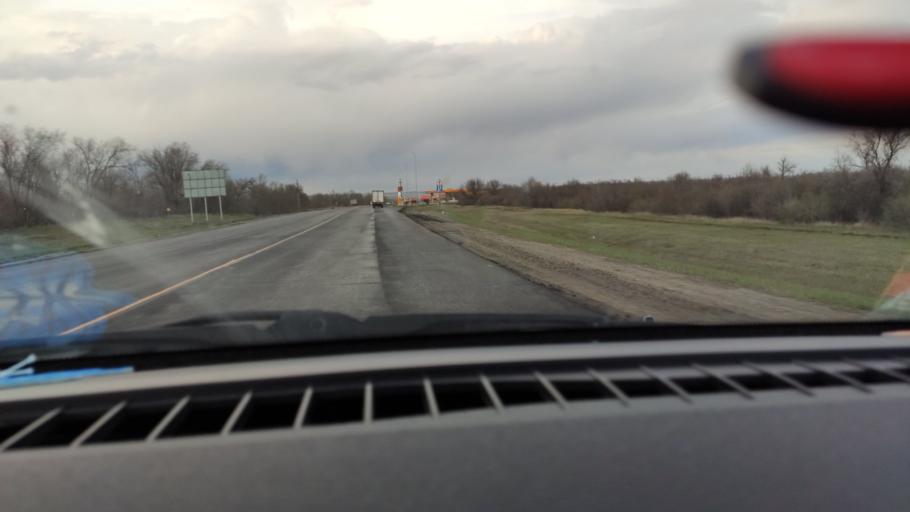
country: RU
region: Saratov
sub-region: Saratovskiy Rayon
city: Saratov
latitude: 51.6837
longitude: 46.0023
